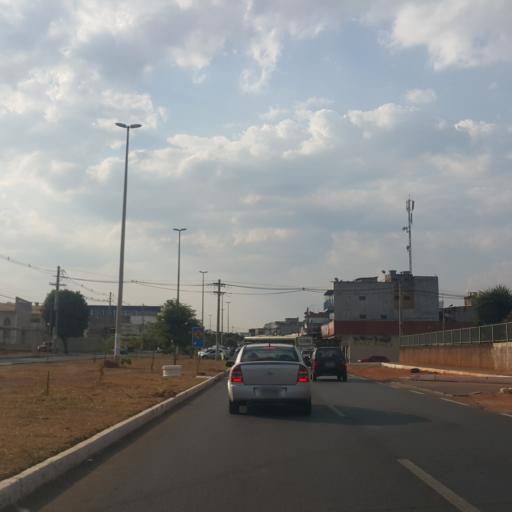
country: BR
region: Federal District
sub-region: Brasilia
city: Brasilia
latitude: -15.8668
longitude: -48.0233
